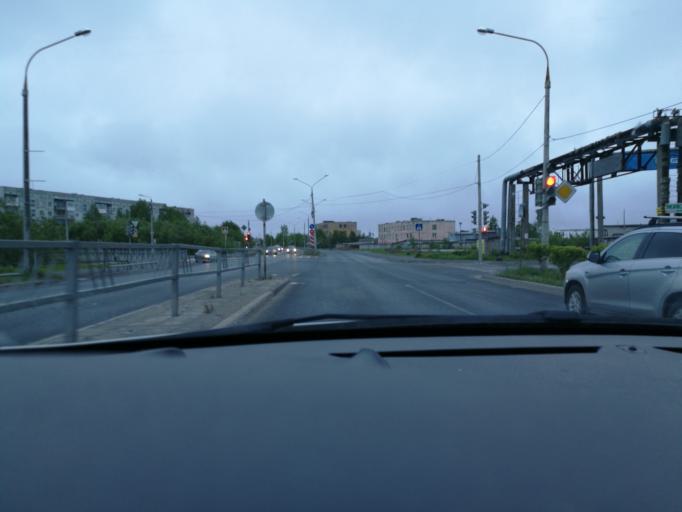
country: RU
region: Arkhangelskaya
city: Severodvinsk
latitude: 64.5669
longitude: 39.7883
